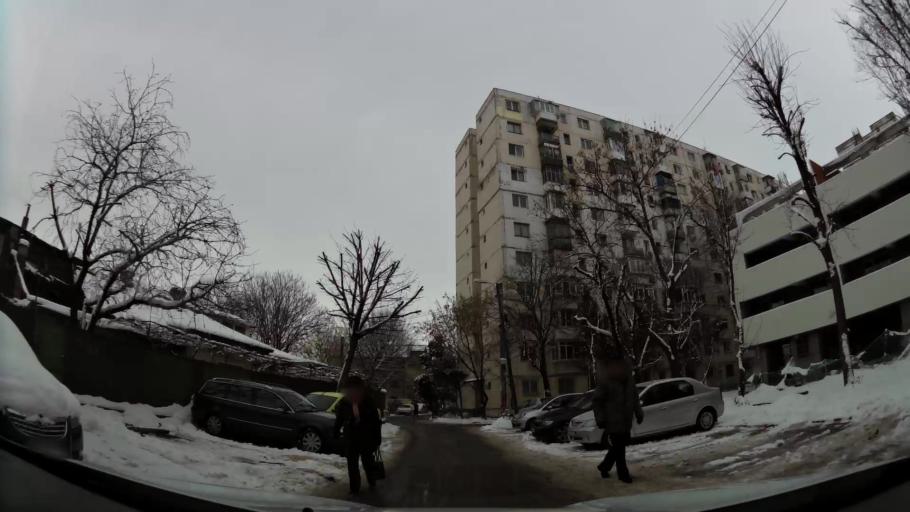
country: RO
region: Bucuresti
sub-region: Municipiul Bucuresti
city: Bucuresti
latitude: 44.3931
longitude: 26.0954
